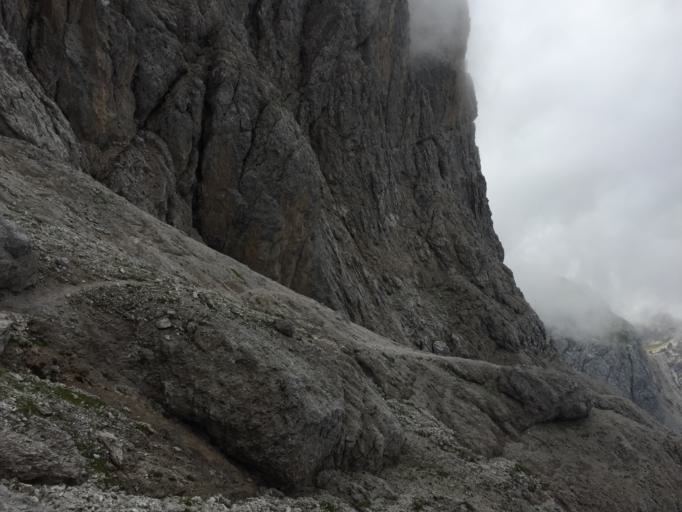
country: IT
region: Veneto
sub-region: Provincia di Belluno
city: Granvilla
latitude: 46.5434
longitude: 12.7366
